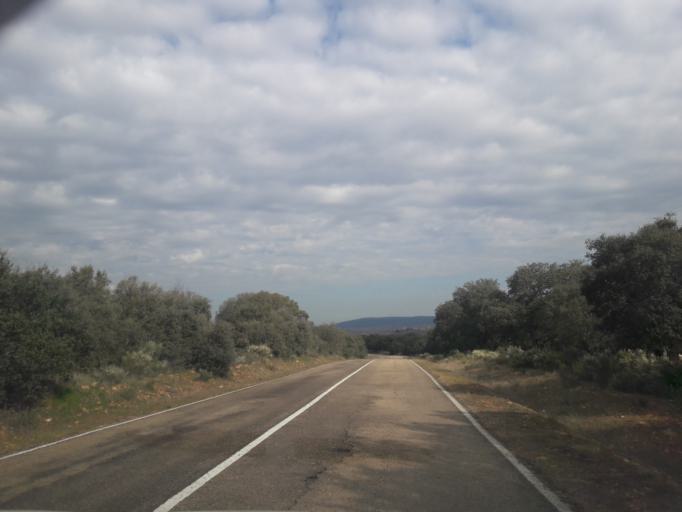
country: ES
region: Castille and Leon
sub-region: Provincia de Salamanca
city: Ciudad Rodrigo
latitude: 40.5655
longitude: -6.5282
